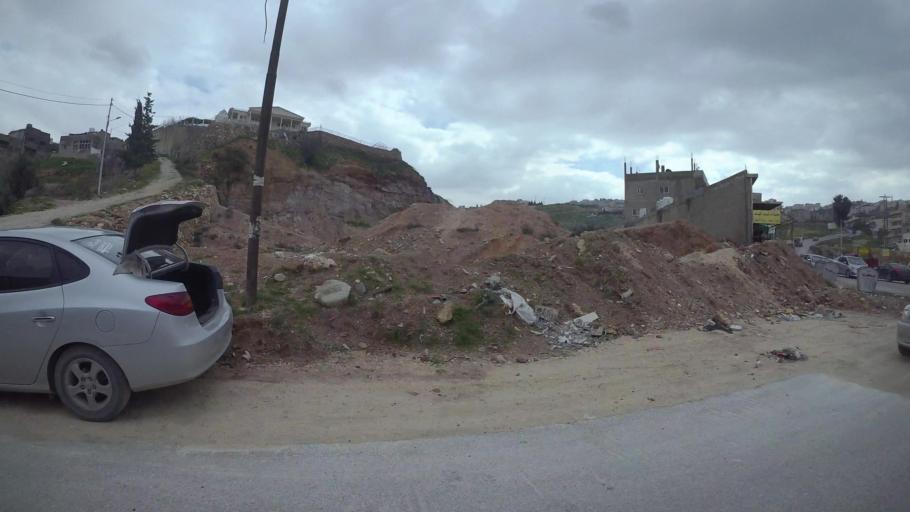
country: JO
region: Amman
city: Al Jubayhah
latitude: 32.0466
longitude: 35.8333
